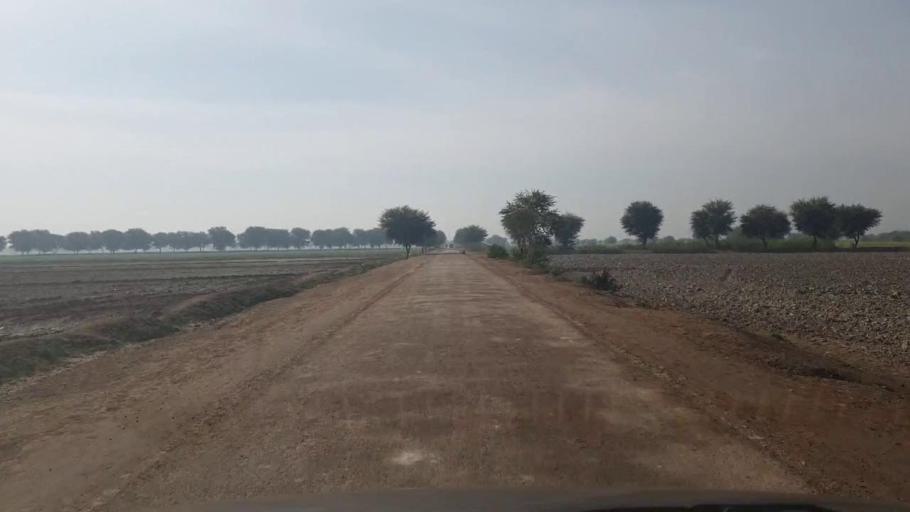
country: PK
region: Sindh
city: Umarkot
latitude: 25.3495
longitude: 69.6763
